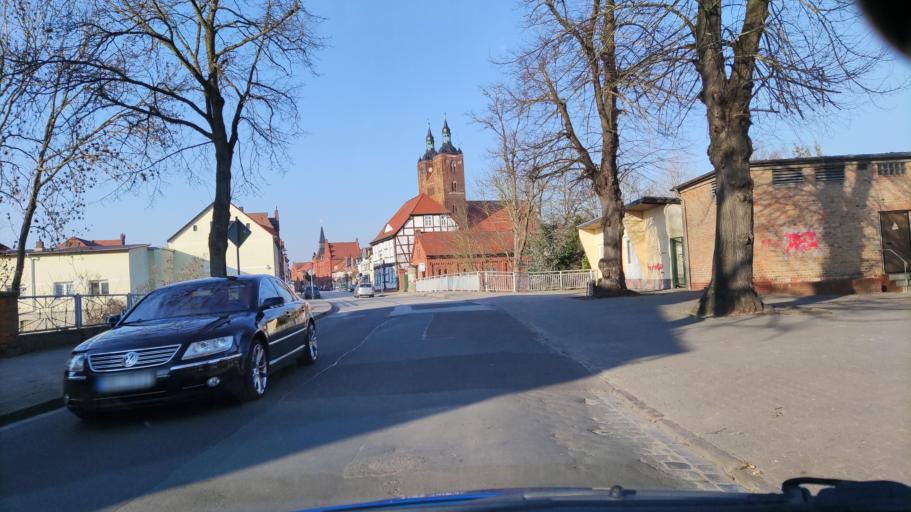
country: DE
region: Saxony-Anhalt
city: Seehausen
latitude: 52.8879
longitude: 11.7524
